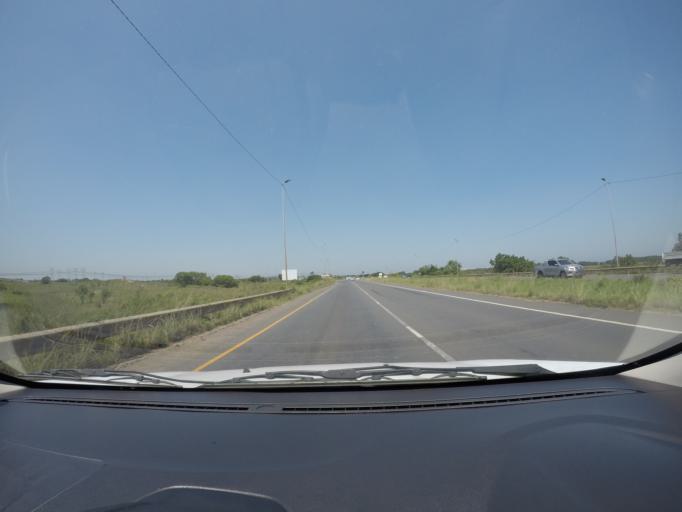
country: ZA
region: KwaZulu-Natal
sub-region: uThungulu District Municipality
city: Richards Bay
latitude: -28.7802
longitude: 31.9881
